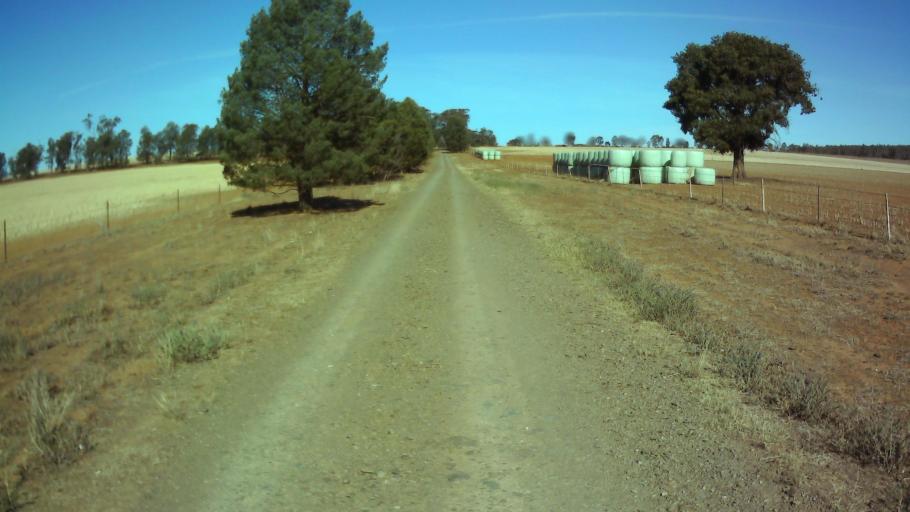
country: AU
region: New South Wales
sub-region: Weddin
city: Grenfell
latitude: -33.7793
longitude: 147.8285
